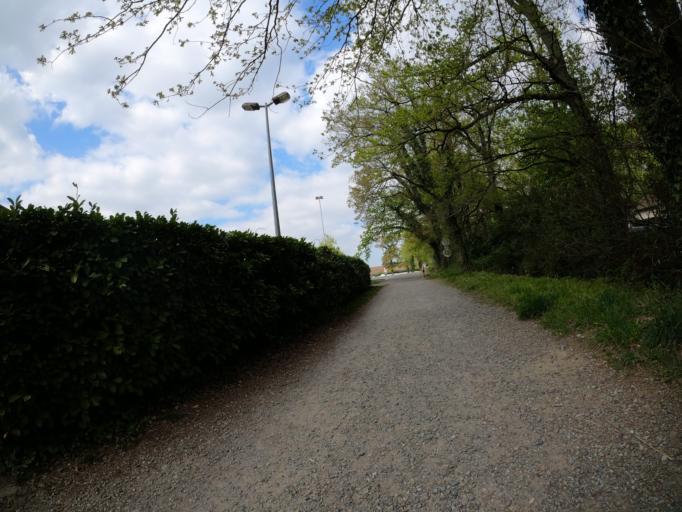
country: FR
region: Aquitaine
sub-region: Departement des Pyrenees-Atlantiques
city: Lons
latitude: 43.3237
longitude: -0.3924
